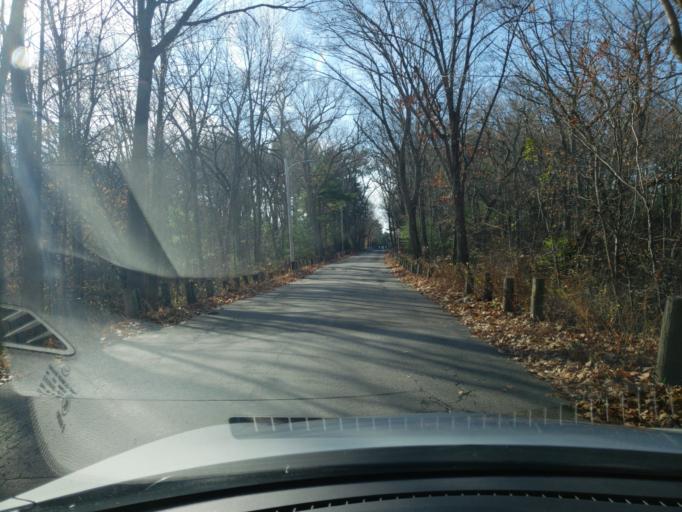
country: US
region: Massachusetts
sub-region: Essex County
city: Andover
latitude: 42.6348
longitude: -71.1470
